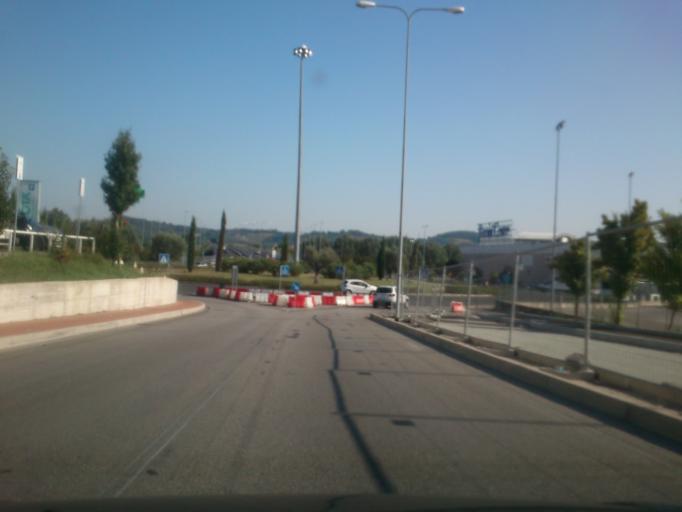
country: IT
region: The Marches
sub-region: Provincia di Pesaro e Urbino
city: Pesaro
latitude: 43.9074
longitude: 12.8692
